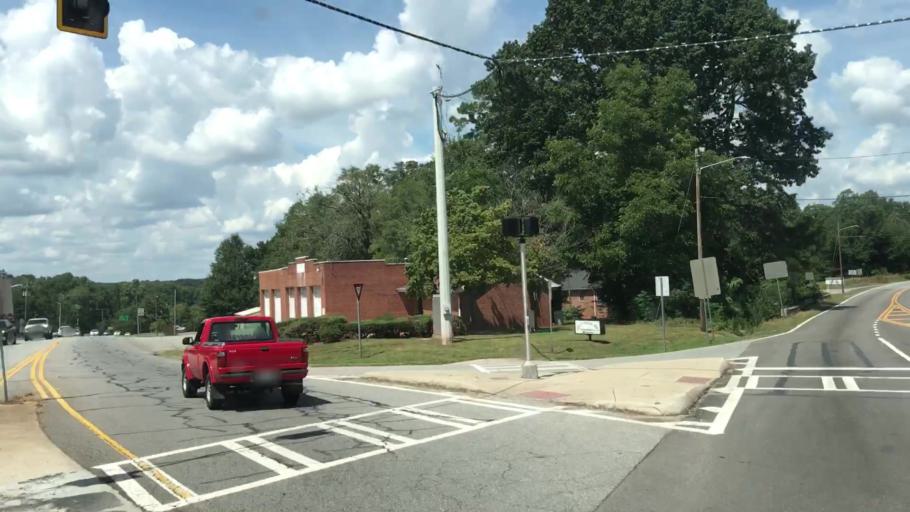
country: US
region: Georgia
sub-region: Oconee County
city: Watkinsville
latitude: 33.8654
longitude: -83.4109
